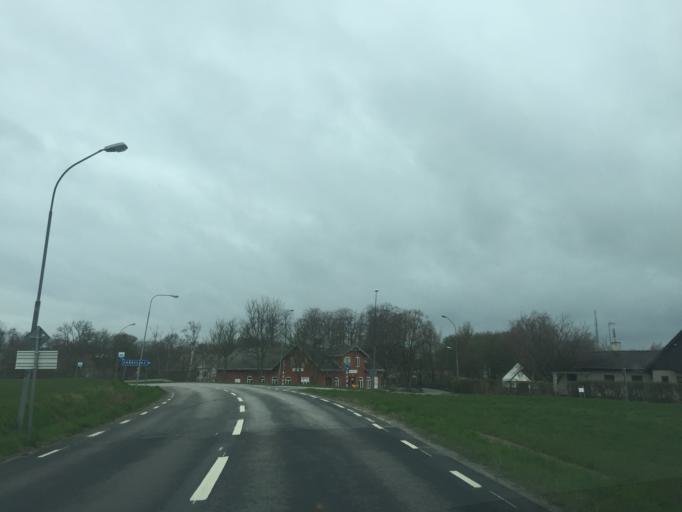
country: SE
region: Skane
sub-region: Skurups Kommun
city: Skivarp
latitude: 55.4258
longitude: 13.5856
